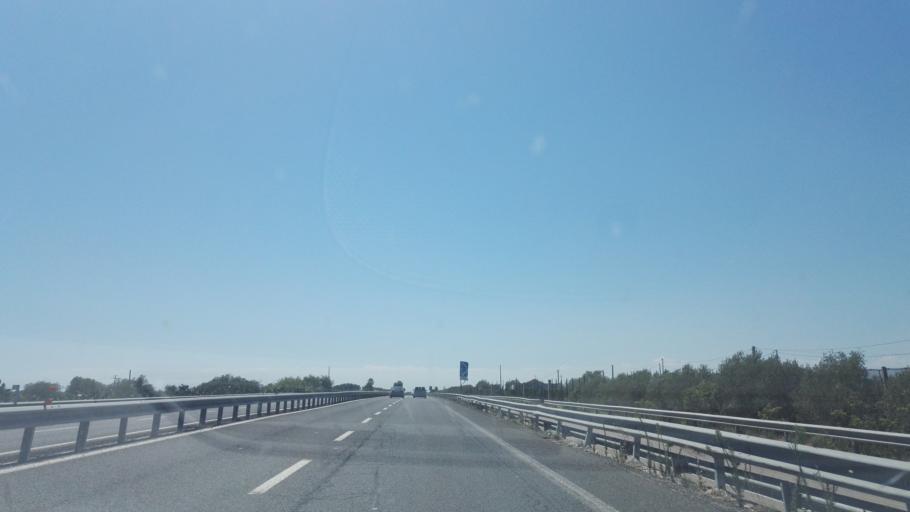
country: IT
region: Apulia
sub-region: Provincia di Taranto
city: Palagiano
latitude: 40.5191
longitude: 17.0160
